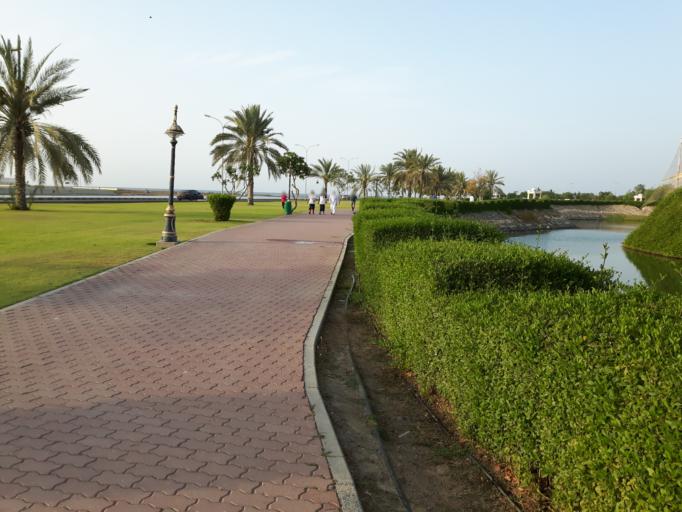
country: OM
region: Al Batinah
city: Al Sohar
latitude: 24.4052
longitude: 56.7145
